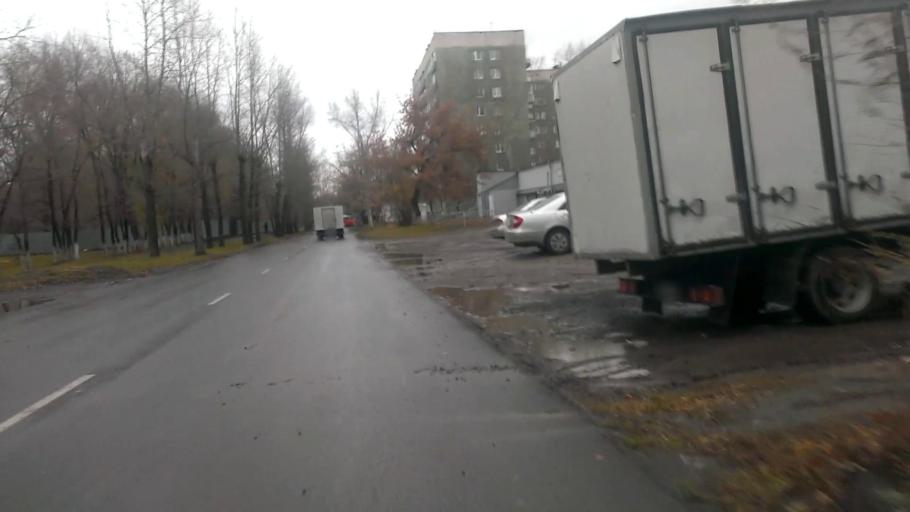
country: RU
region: Altai Krai
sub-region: Gorod Barnaulskiy
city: Barnaul
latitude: 53.3628
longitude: 83.6874
